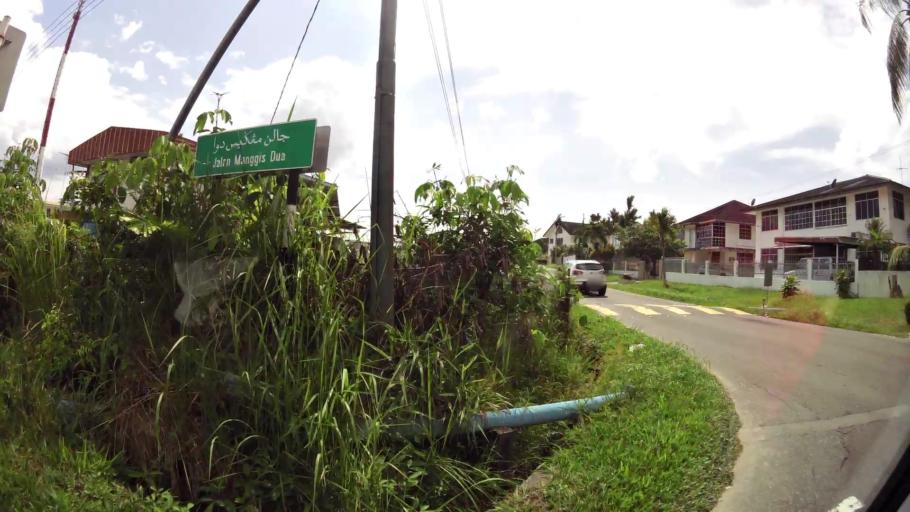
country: BN
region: Brunei and Muara
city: Bandar Seri Begawan
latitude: 4.9579
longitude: 114.9647
